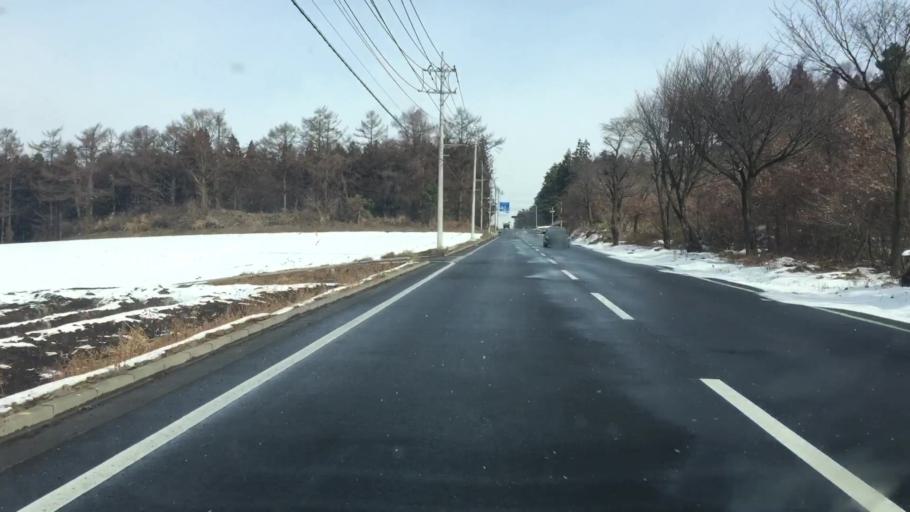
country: JP
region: Gunma
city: Numata
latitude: 36.6203
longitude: 139.0865
